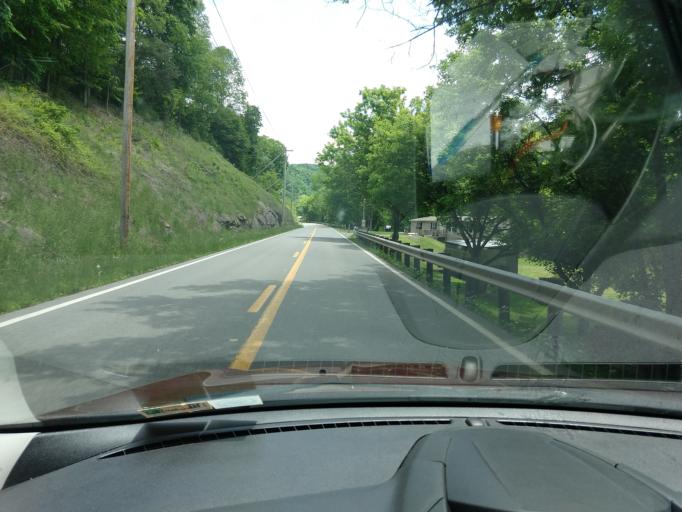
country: US
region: West Virginia
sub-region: Gilmer County
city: Glenville
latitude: 38.8783
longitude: -80.7102
